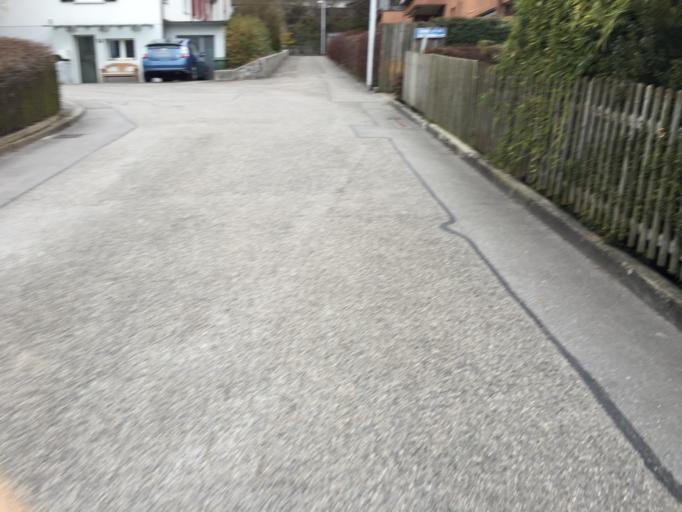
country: CH
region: Bern
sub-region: Bern-Mittelland District
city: Koniz
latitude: 46.9236
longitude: 7.4095
